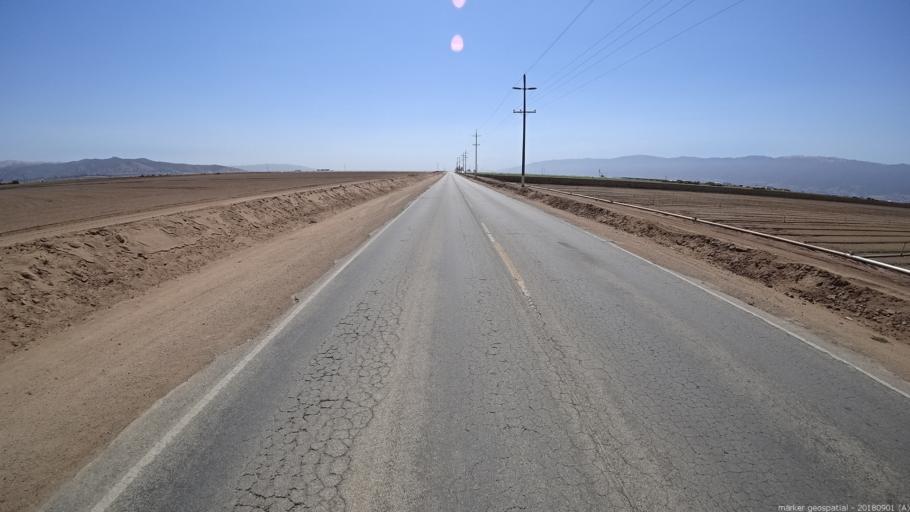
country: US
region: California
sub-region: Monterey County
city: Chualar
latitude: 36.5945
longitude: -121.5056
